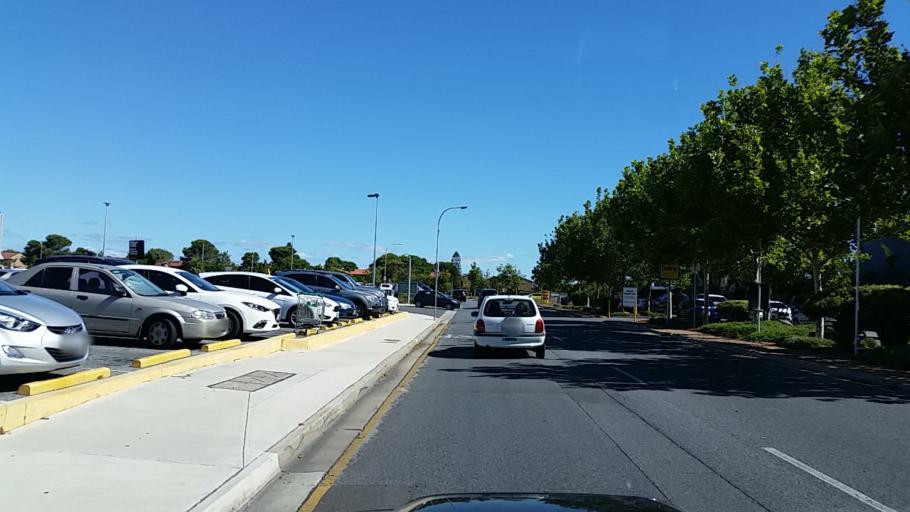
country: AU
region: South Australia
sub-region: Charles Sturt
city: West Lakes Shore
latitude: -34.8801
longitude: 138.4893
